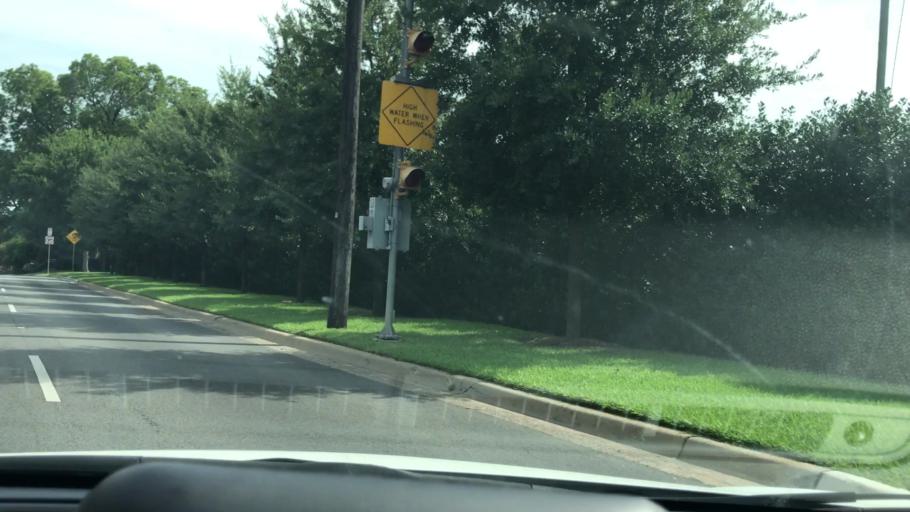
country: US
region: Texas
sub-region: Dallas County
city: University Park
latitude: 32.8800
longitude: -96.8211
